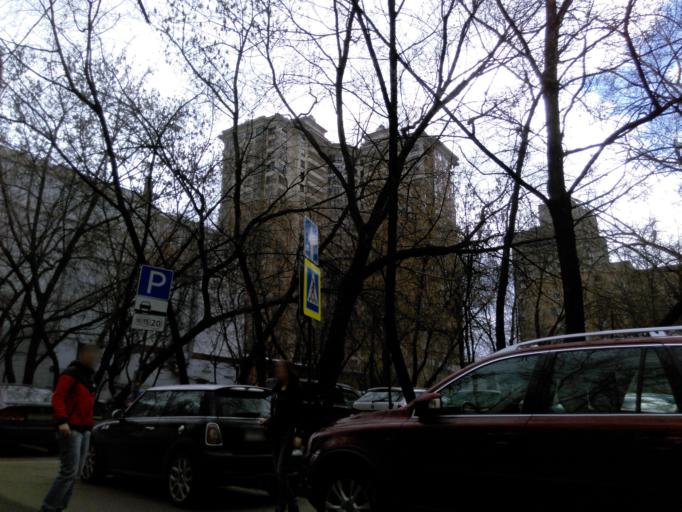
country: RU
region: Moskovskaya
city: Dorogomilovo
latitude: 55.7704
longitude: 37.5759
